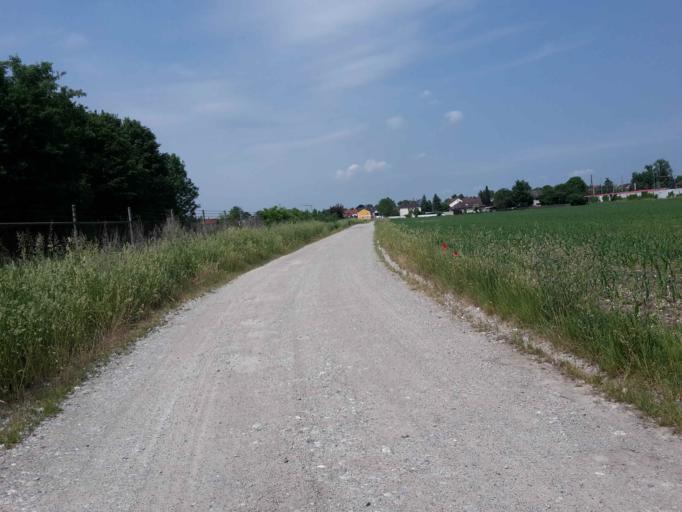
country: DE
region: Bavaria
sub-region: Upper Bavaria
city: Maisach
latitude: 48.2128
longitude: 11.2663
